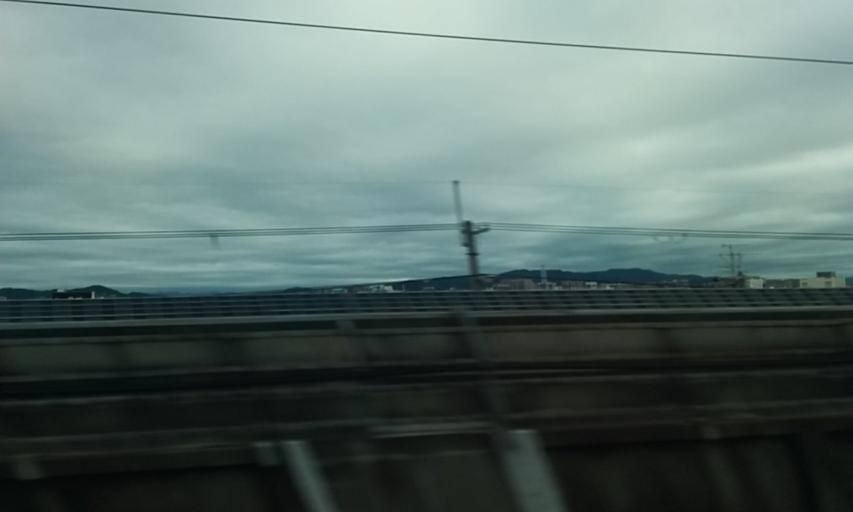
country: JP
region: Hyogo
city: Itami
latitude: 34.7686
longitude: 135.4095
